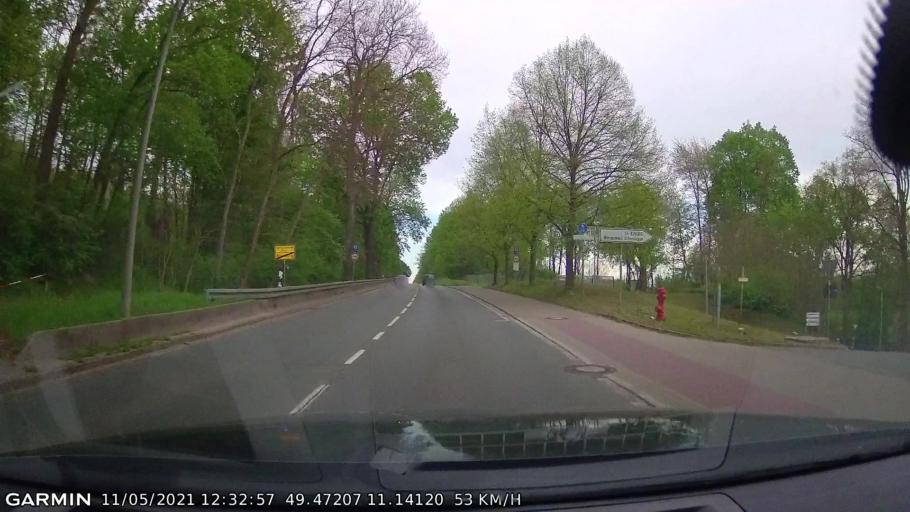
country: DE
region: Bavaria
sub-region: Regierungsbezirk Mittelfranken
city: Schwaig
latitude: 49.4721
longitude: 11.1414
